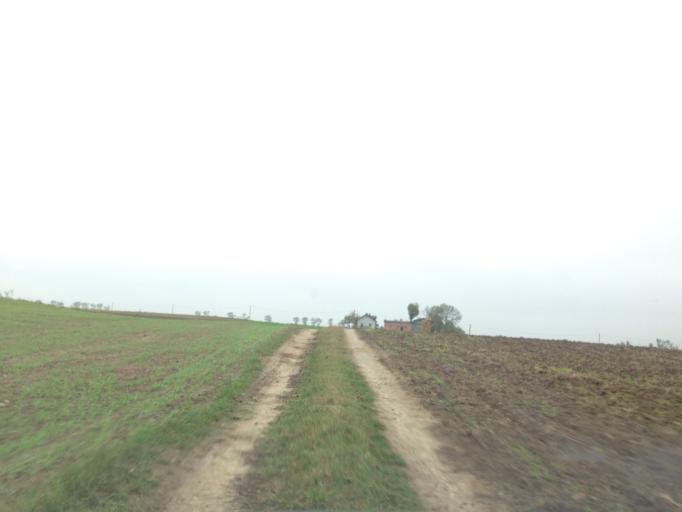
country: PL
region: Kujawsko-Pomorskie
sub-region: Powiat brodnicki
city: Gorzno
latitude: 53.2093
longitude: 19.6161
